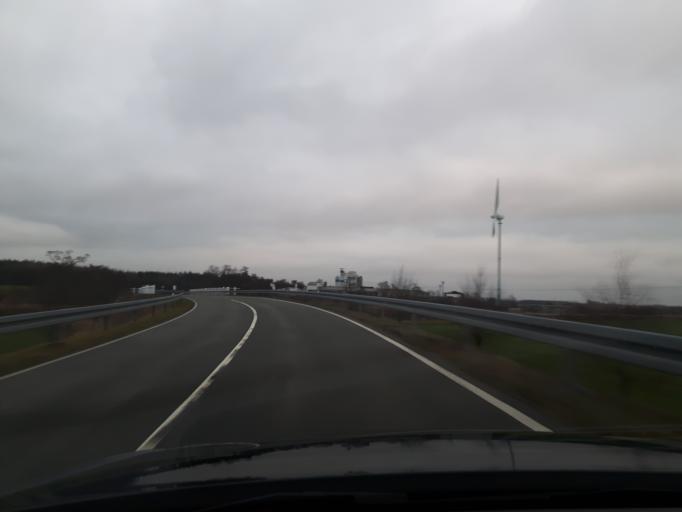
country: DE
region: Mecklenburg-Vorpommern
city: Tribsees
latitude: 54.0684
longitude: 12.7161
